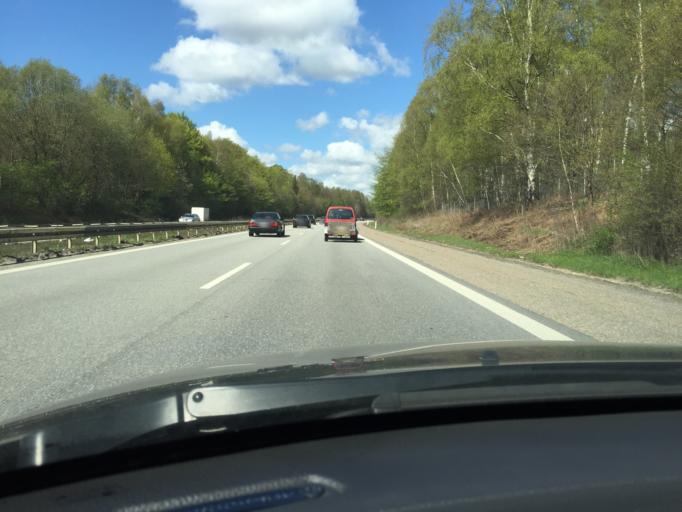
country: DK
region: Capital Region
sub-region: Fureso Kommune
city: Vaerlose
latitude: 55.7919
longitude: 12.3841
